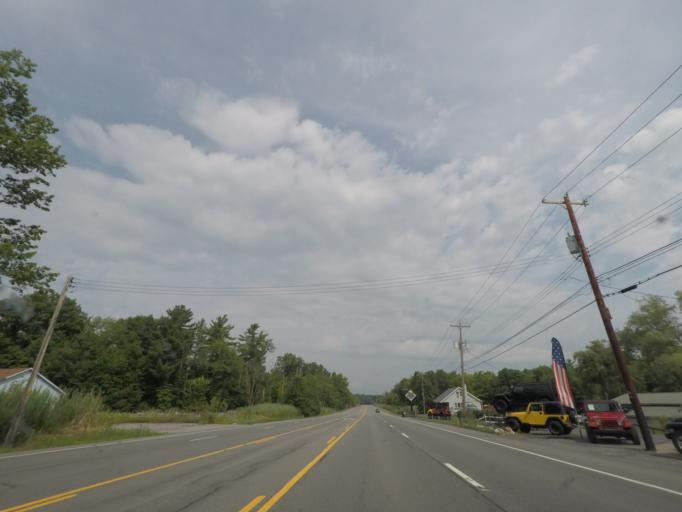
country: US
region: New York
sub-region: Saratoga County
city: Country Knolls
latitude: 42.9128
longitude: -73.7842
